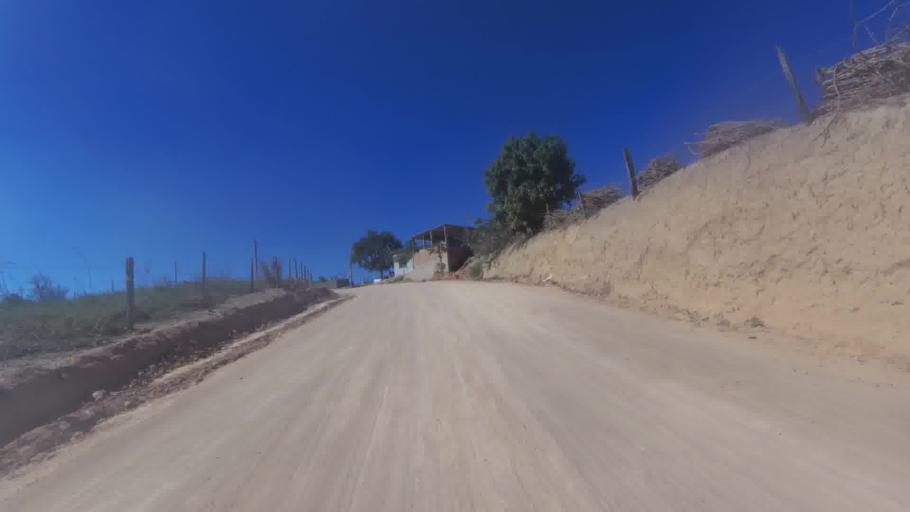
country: BR
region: Espirito Santo
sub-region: Marataizes
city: Marataizes
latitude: -21.1457
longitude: -40.9834
